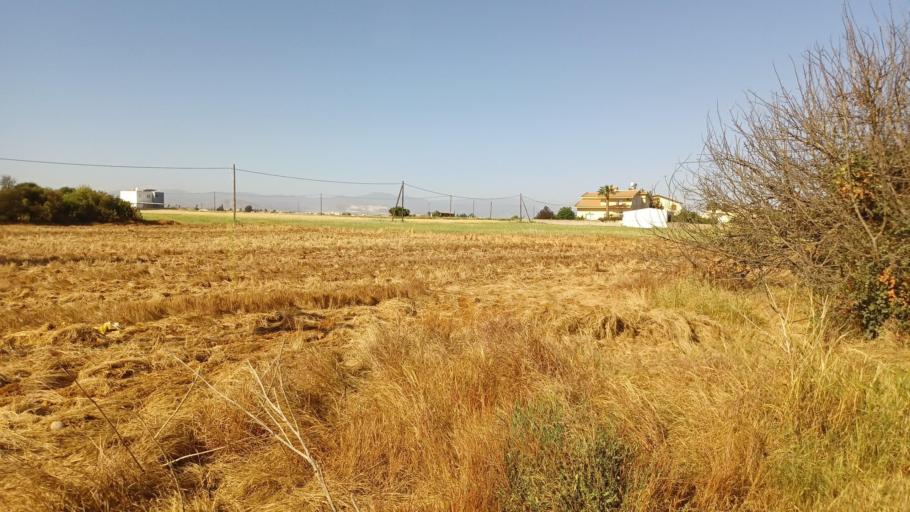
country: CY
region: Lefkosia
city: Kokkinotrimithia
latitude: 35.1451
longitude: 33.2103
